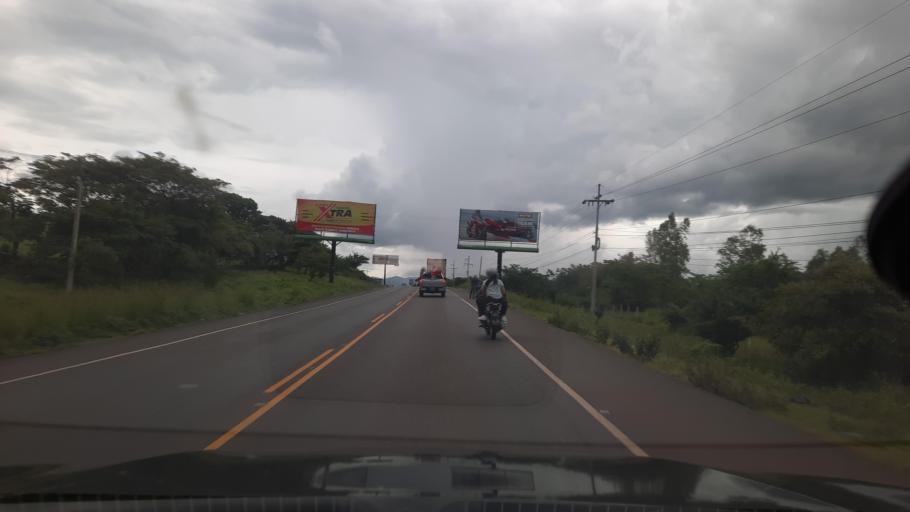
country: HN
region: Choluteca
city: Ciudad Choluteca
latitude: 13.3251
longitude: -87.2183
